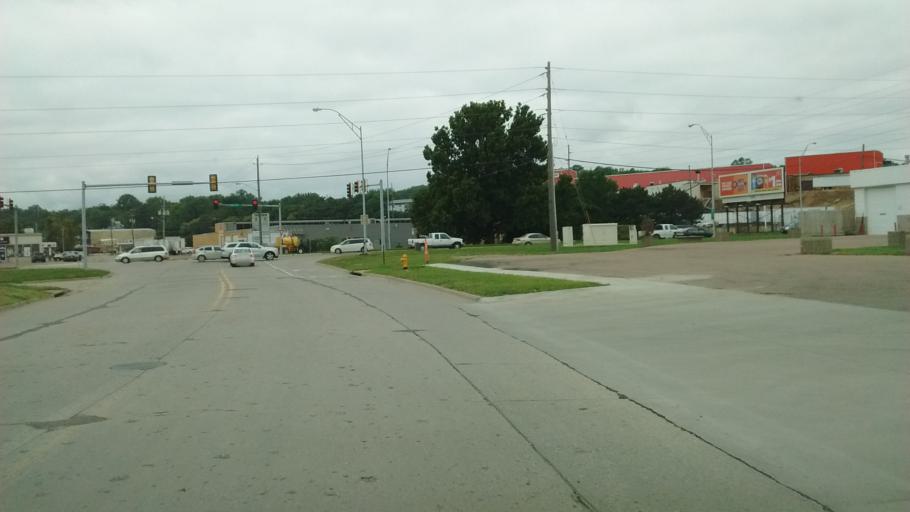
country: US
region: Nebraska
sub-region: Dakota County
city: South Sioux City
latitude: 42.4943
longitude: -96.4232
